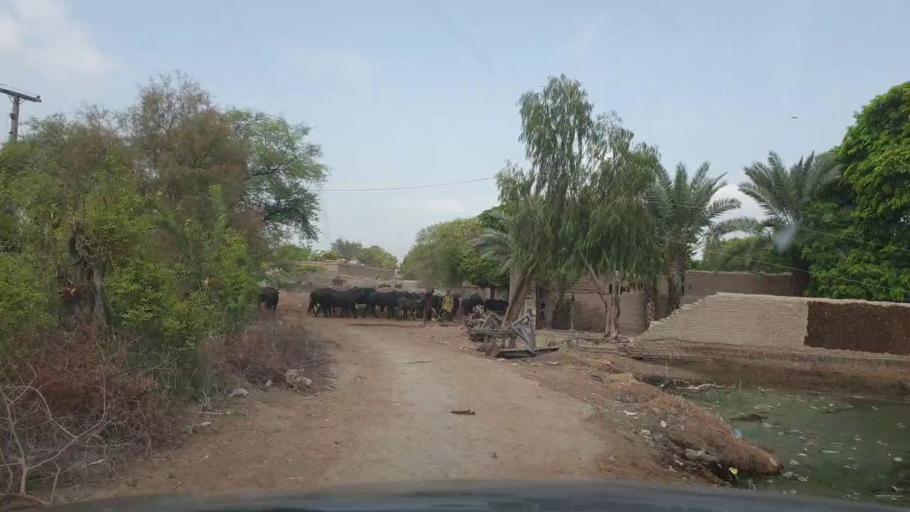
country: PK
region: Sindh
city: Ratodero
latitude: 27.8581
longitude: 68.2899
